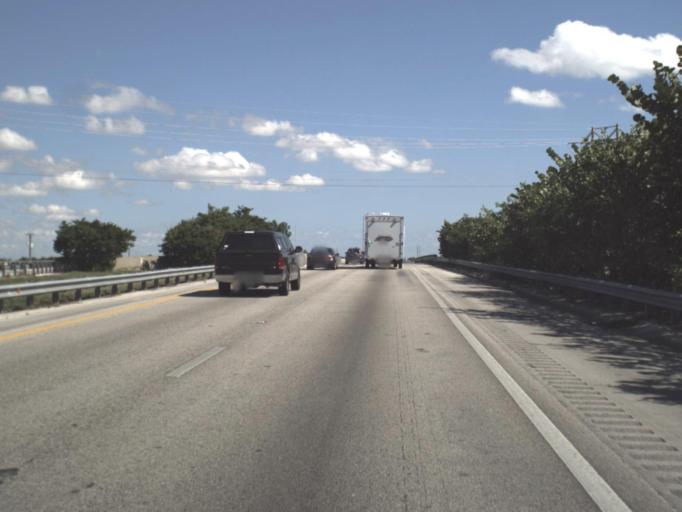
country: US
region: Florida
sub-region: Miami-Dade County
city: Homestead
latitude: 25.4618
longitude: -80.4631
